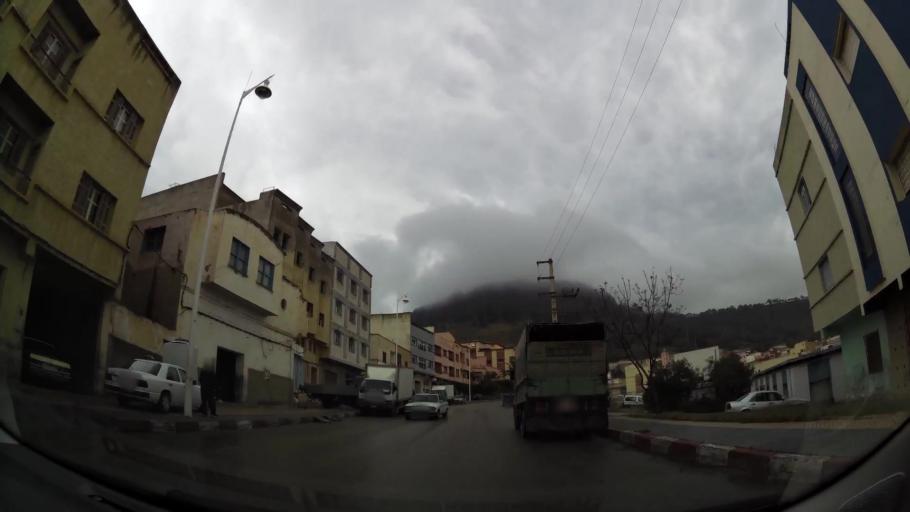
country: MA
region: Oriental
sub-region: Nador
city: Nador
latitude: 35.1530
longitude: -3.0073
